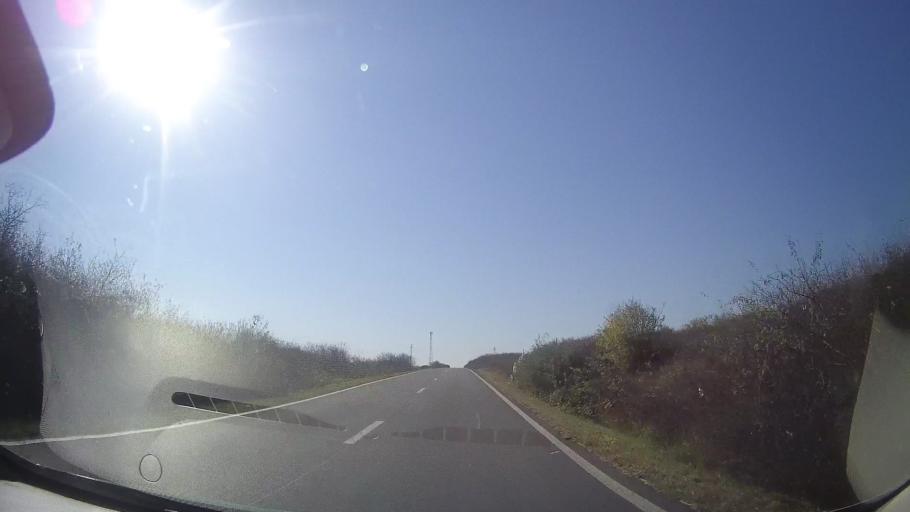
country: RO
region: Timis
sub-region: Comuna Belint
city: Belint
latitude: 45.7690
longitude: 21.7291
